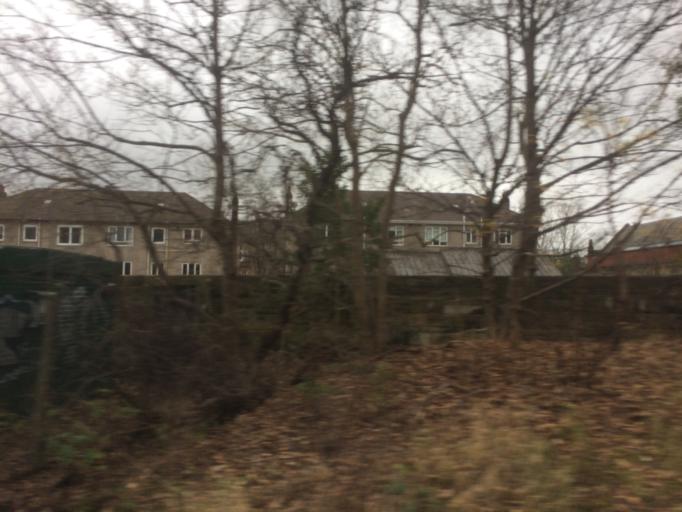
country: GB
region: Scotland
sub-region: East Renfrewshire
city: Clarkston
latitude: 55.8166
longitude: -4.2643
